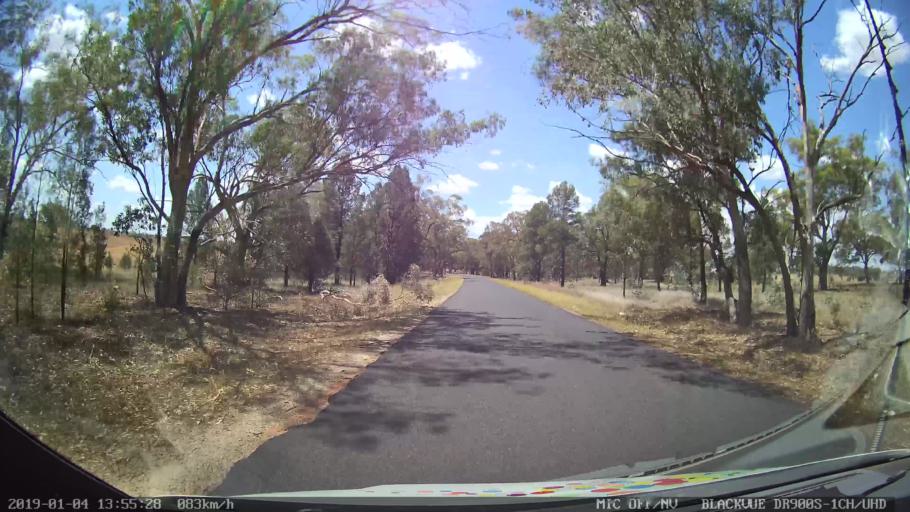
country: AU
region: New South Wales
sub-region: Dubbo Municipality
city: Dubbo
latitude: -32.3618
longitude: 148.5877
